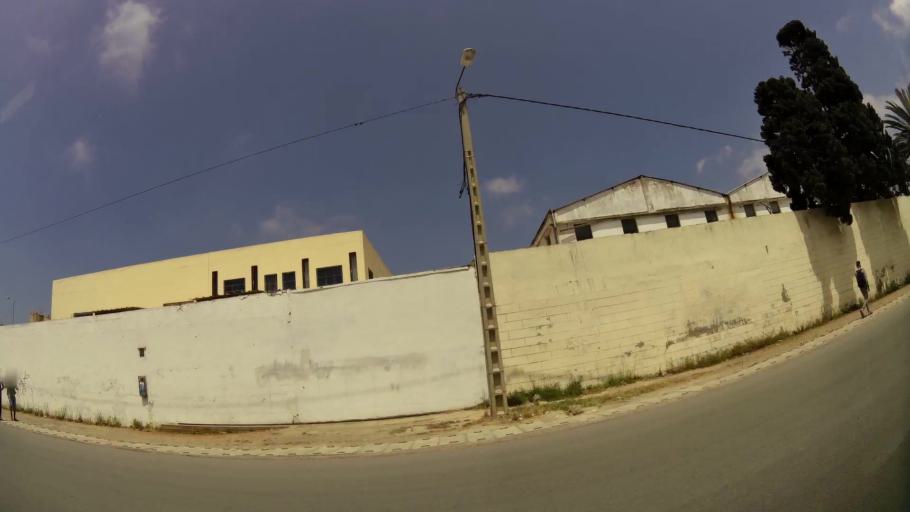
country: MA
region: Rabat-Sale-Zemmour-Zaer
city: Sale
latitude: 34.0600
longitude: -6.7911
